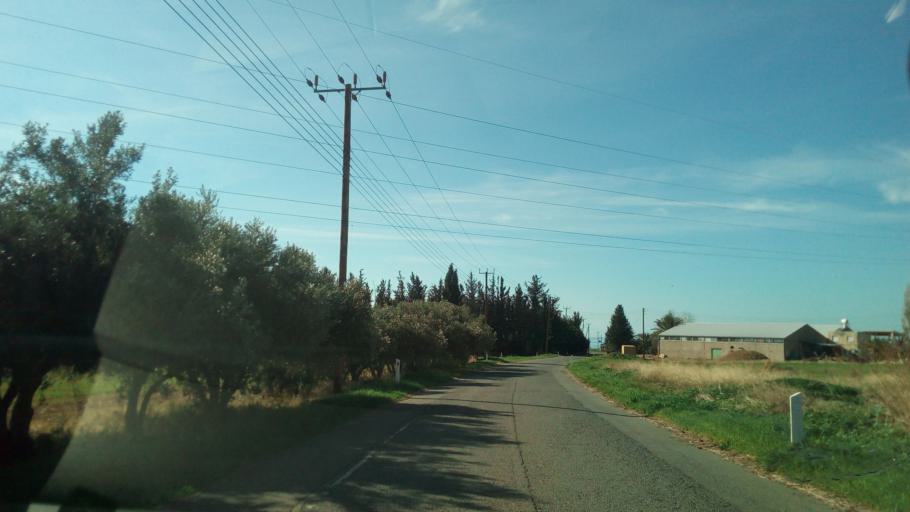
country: CY
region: Limassol
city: Pissouri
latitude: 34.7139
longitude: 32.5866
